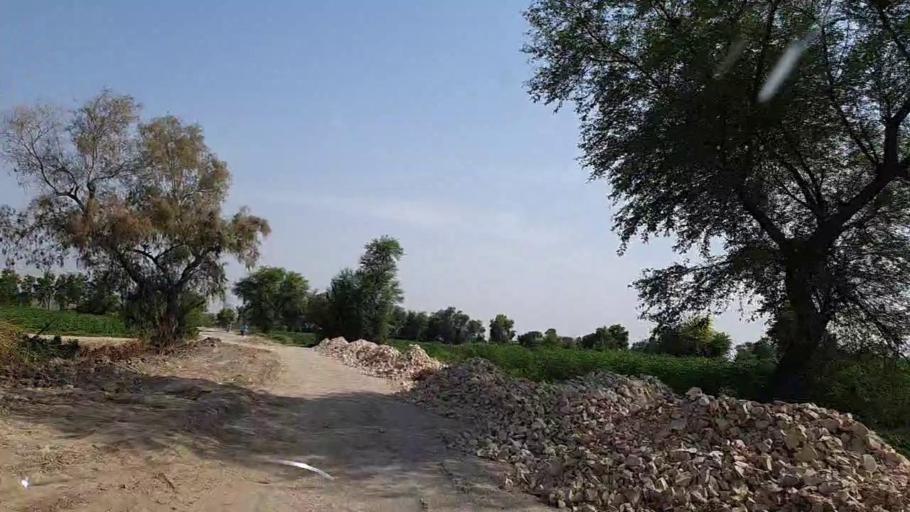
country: PK
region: Sindh
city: Khanpur
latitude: 27.7442
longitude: 69.3415
